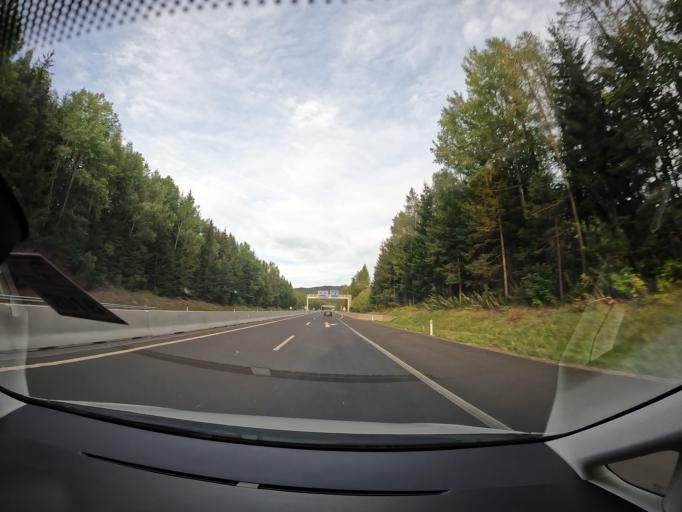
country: AT
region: Carinthia
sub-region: Politischer Bezirk Wolfsberg
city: Preitenegg
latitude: 46.9665
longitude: 14.9443
